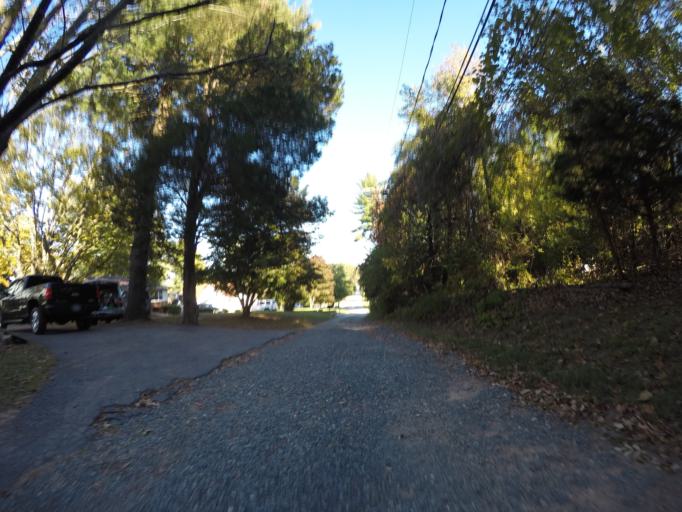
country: US
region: Maryland
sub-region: Howard County
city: Ellicott City
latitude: 39.2959
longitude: -76.8036
